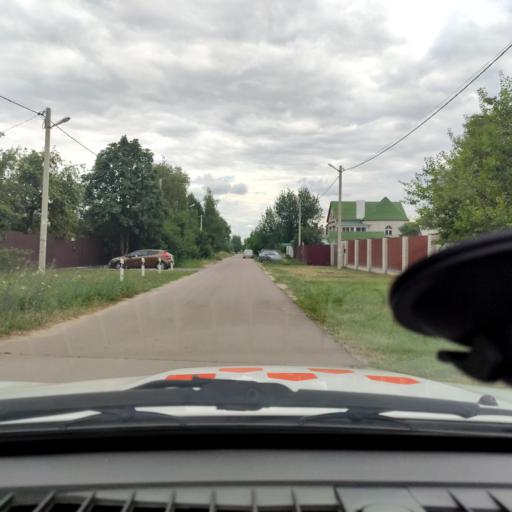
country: RU
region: Voronezj
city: Ramon'
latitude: 51.8294
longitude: 39.2595
